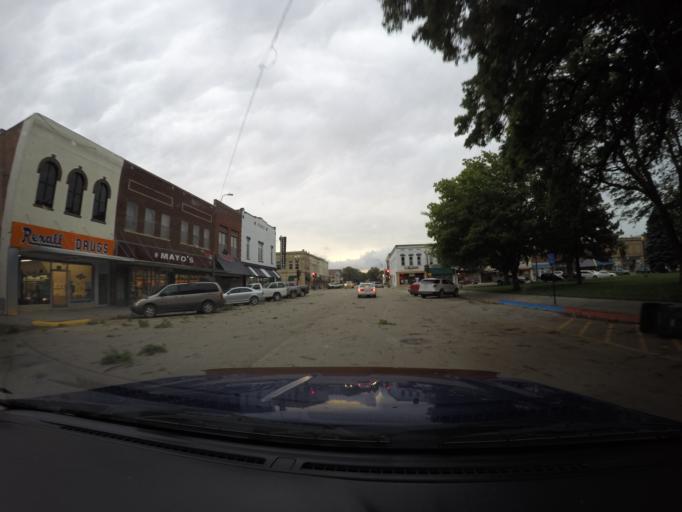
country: US
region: Kansas
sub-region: Clay County
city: Clay Center
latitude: 39.3767
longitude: -97.1264
